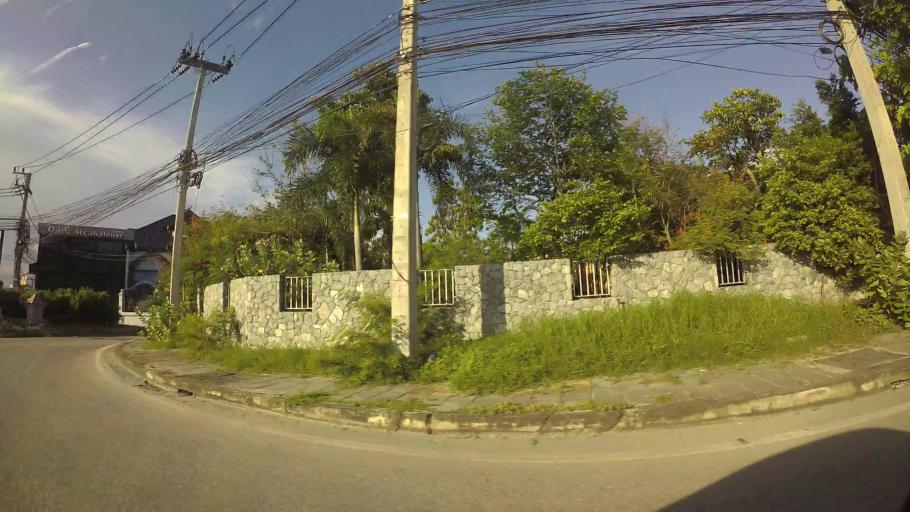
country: TH
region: Rayong
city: Rayong
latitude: 12.6847
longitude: 101.2854
